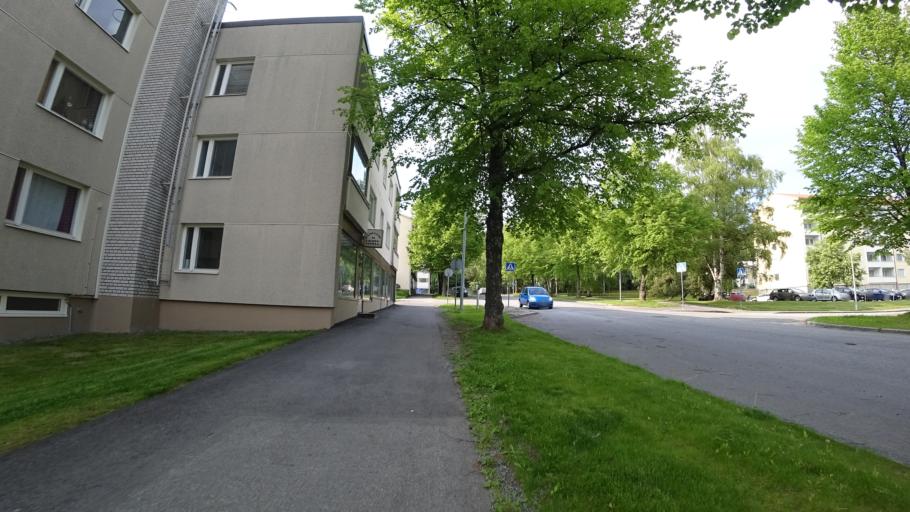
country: FI
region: Pirkanmaa
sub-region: Tampere
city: Pirkkala
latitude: 61.4984
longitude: 23.6381
